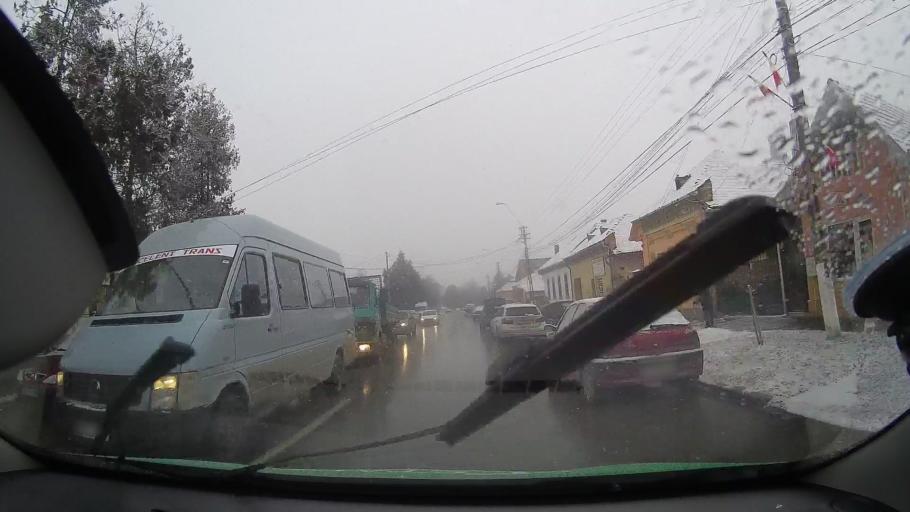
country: RO
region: Alba
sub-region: Municipiul Aiud
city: Aiud
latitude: 46.3103
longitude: 23.7293
